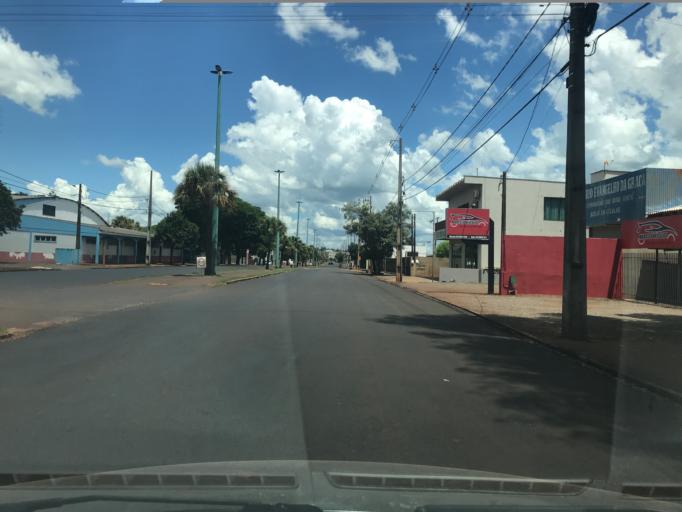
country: BR
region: Parana
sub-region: Palotina
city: Palotina
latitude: -24.2734
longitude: -53.8417
